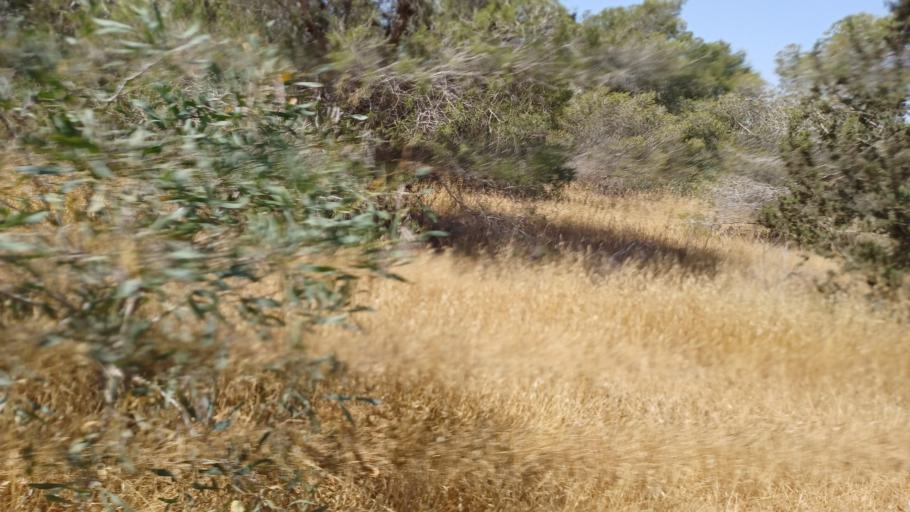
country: CY
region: Ammochostos
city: Paralimni
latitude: 35.0046
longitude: 33.9583
